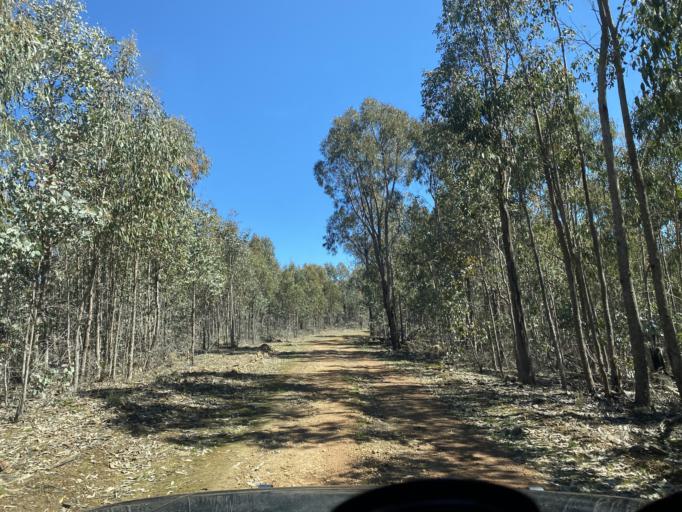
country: AU
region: Victoria
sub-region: Benalla
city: Benalla
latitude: -36.7255
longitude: 146.1815
